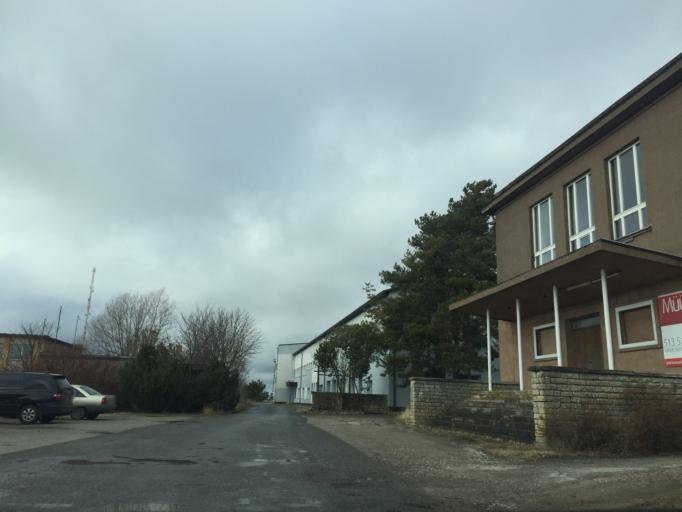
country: EE
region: Laeaene
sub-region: Haapsalu linn
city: Haapsalu
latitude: 58.9572
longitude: 23.5244
